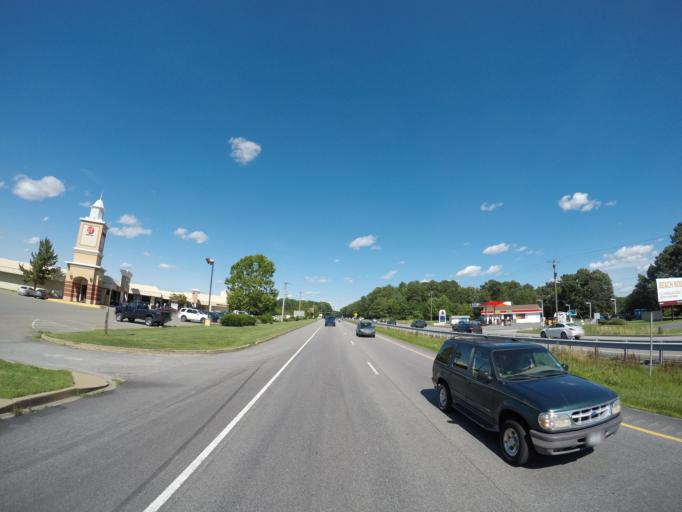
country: US
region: Maryland
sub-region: Queen Anne's County
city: Grasonville
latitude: 38.9817
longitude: -76.1621
